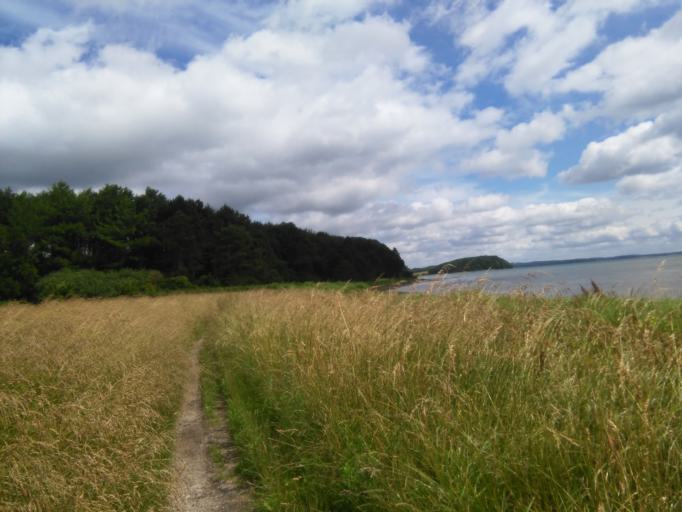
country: DK
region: Central Jutland
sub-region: Arhus Kommune
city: Logten
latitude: 56.2626
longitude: 10.3451
